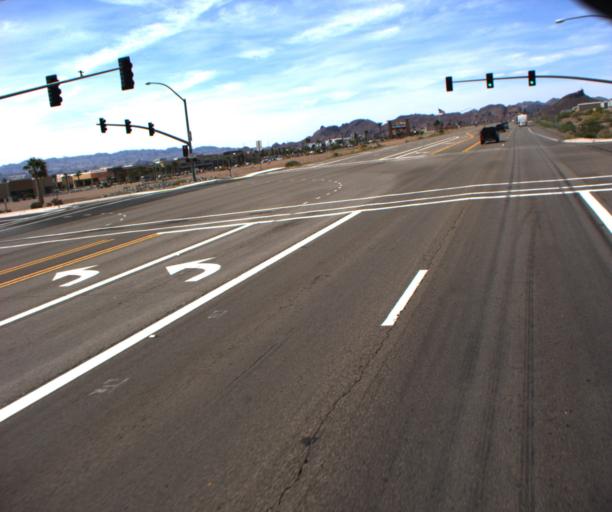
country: US
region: Arizona
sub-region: Mohave County
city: Desert Hills
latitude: 34.5671
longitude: -114.3625
